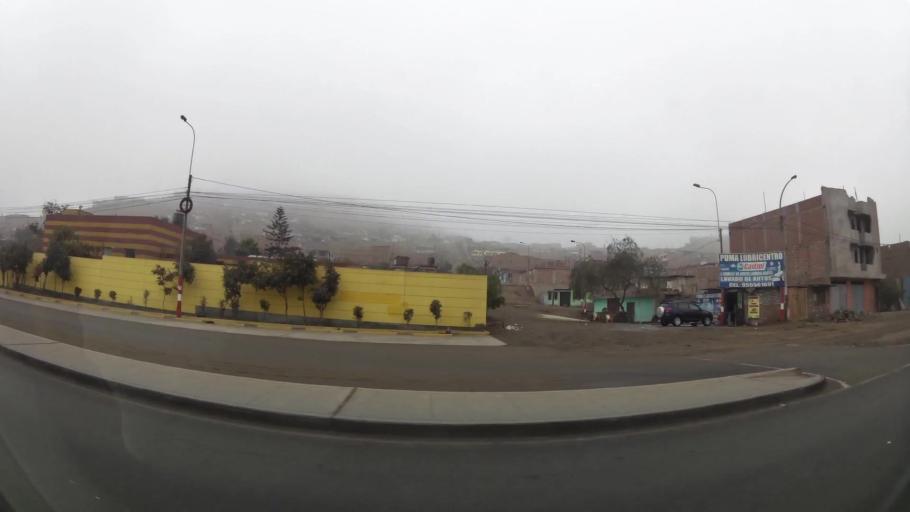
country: PE
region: Lima
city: Ventanilla
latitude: -11.8430
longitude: -77.1163
